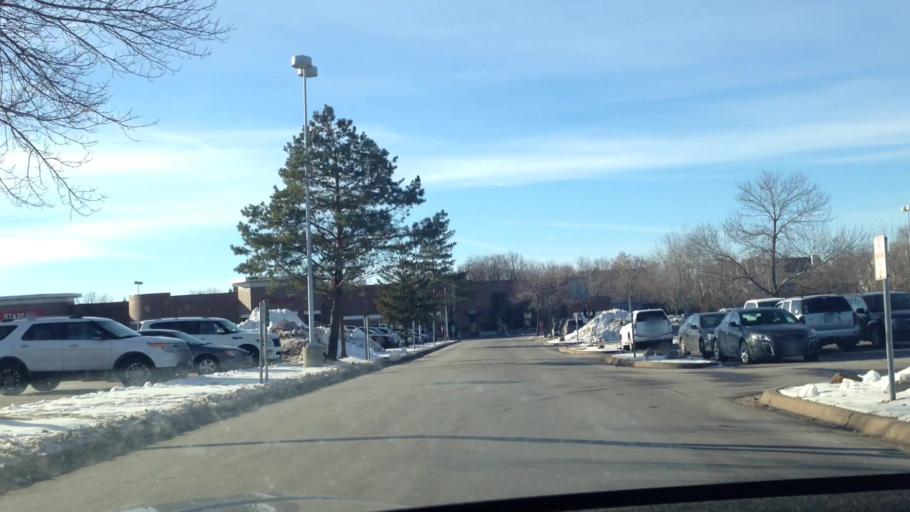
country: US
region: Minnesota
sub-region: Hennepin County
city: Minnetonka Mills
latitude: 44.9725
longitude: -93.4236
